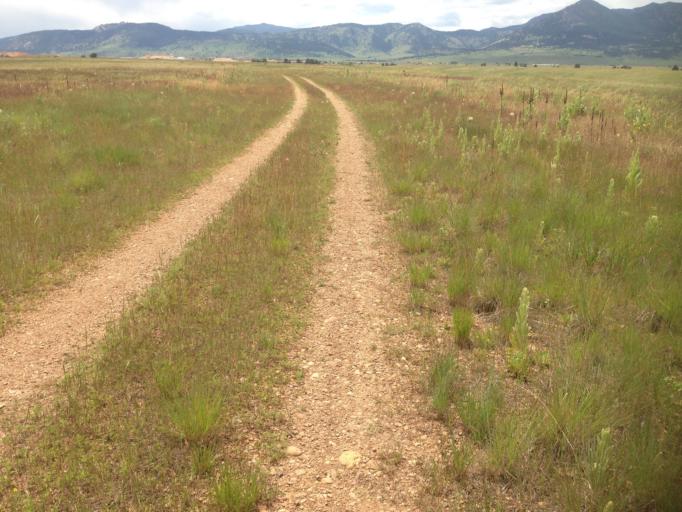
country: US
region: Colorado
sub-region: Boulder County
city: Superior
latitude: 39.9016
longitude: -105.2126
